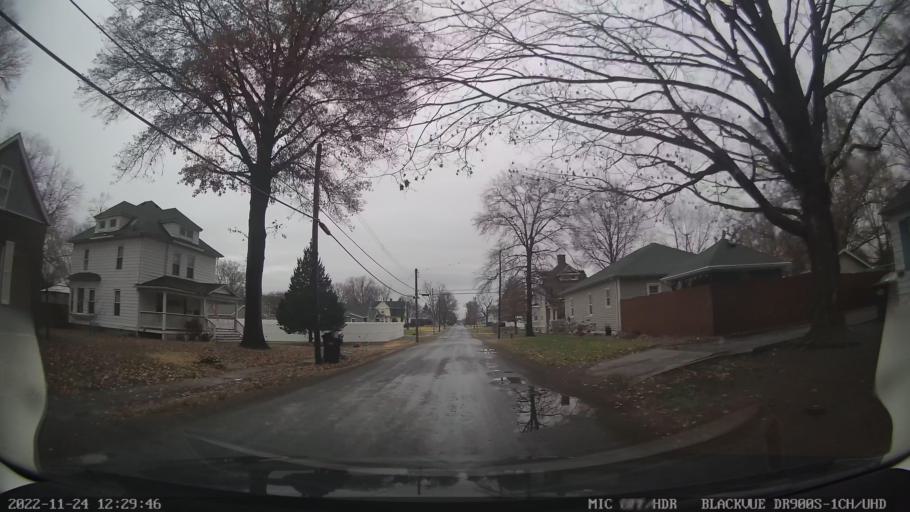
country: US
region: Illinois
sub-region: Macoupin County
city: Staunton
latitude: 39.0145
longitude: -89.7874
